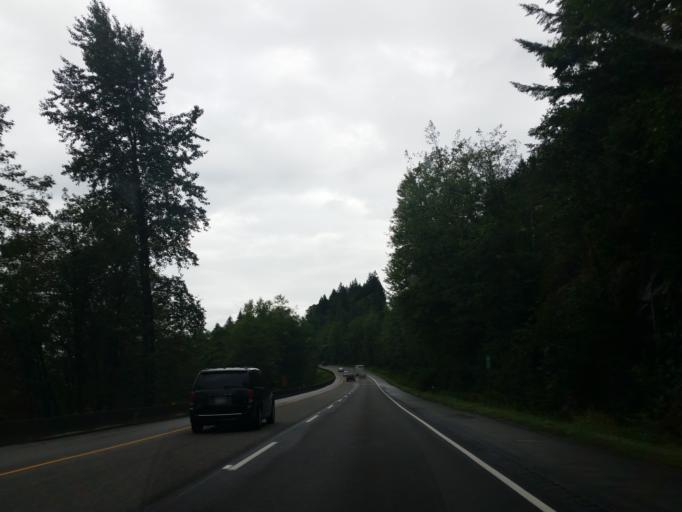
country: CA
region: British Columbia
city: Agassiz
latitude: 49.2456
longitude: -121.6772
